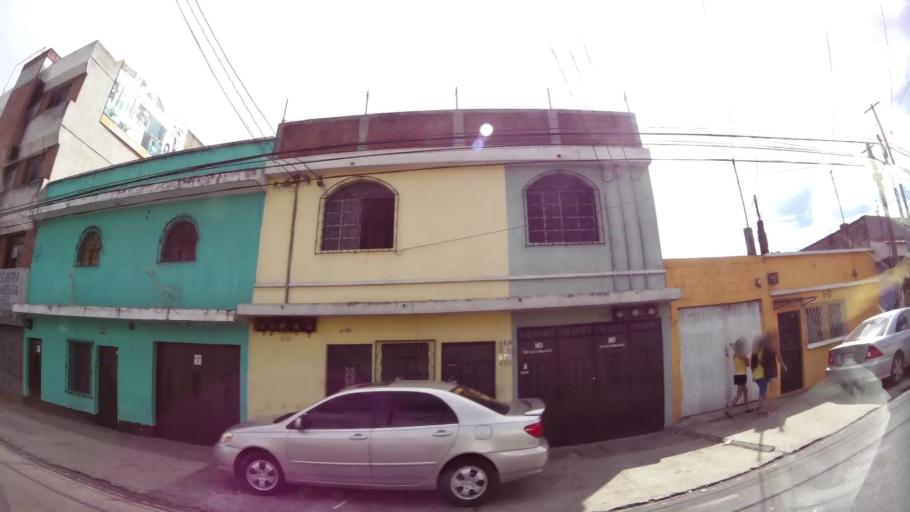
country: GT
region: Guatemala
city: Mixco
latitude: 14.6612
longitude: -90.5731
